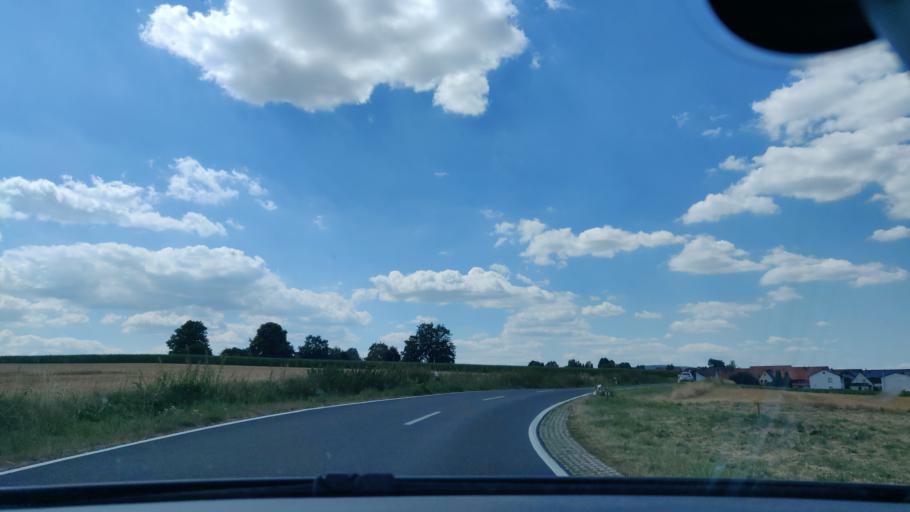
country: DE
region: Hesse
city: Fritzlar
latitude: 51.1537
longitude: 9.3181
